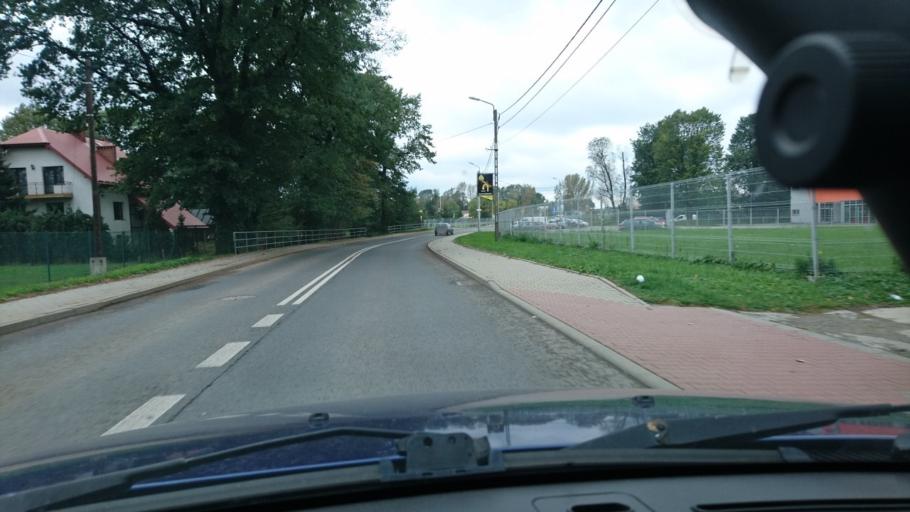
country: PL
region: Silesian Voivodeship
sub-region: Powiat bielski
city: Mazancowice
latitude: 49.8212
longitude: 18.9784
